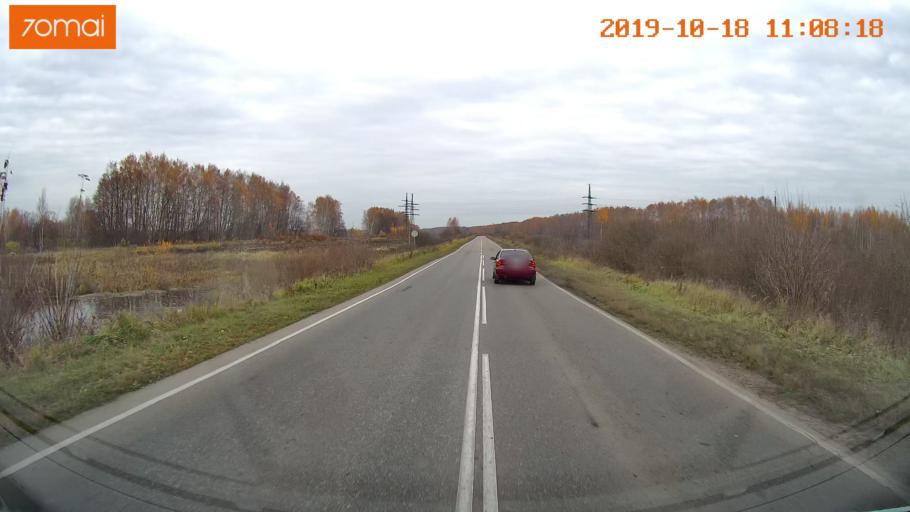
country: RU
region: Tula
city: Kimovsk
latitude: 53.9358
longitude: 38.5380
